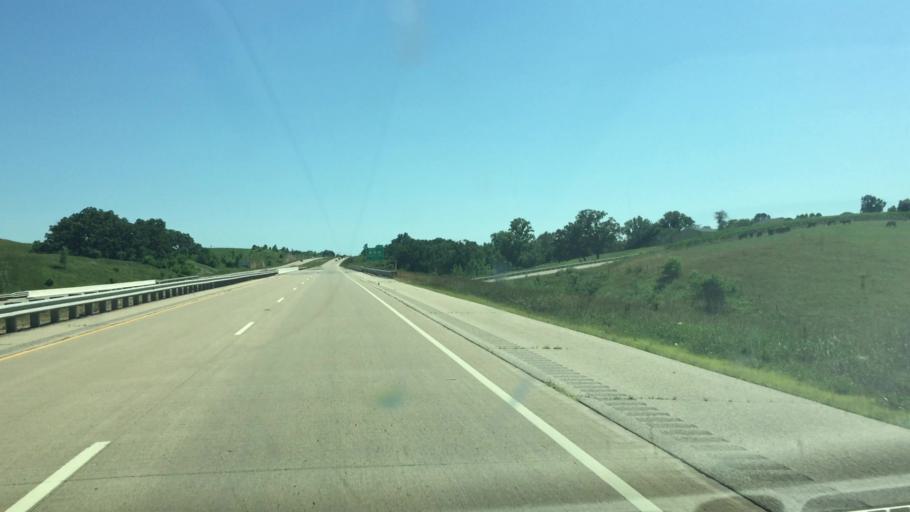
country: US
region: Wisconsin
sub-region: Grant County
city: Dickeyville
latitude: 42.6339
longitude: -90.5799
